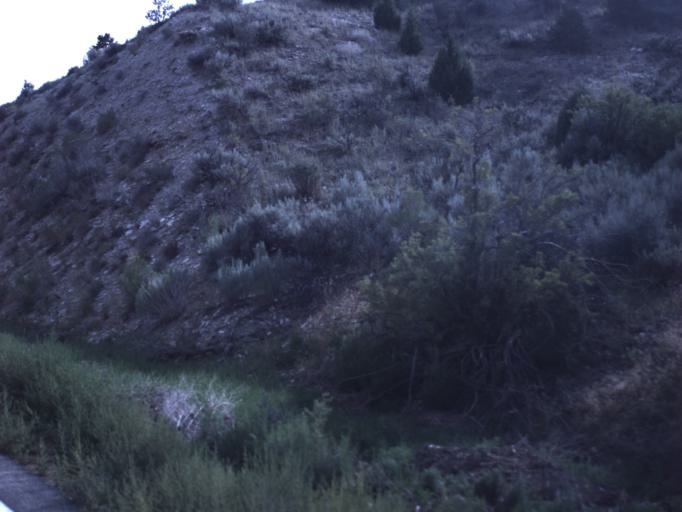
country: US
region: Utah
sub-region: Duchesne County
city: Duchesne
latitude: 40.0706
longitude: -110.5124
